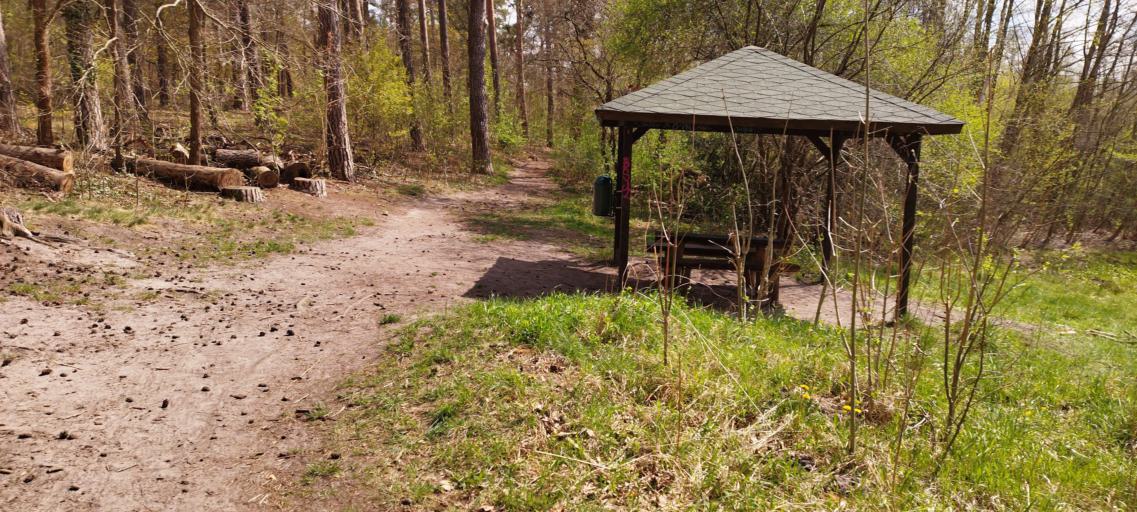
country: DE
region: Brandenburg
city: Erkner
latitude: 52.4202
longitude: 13.7660
